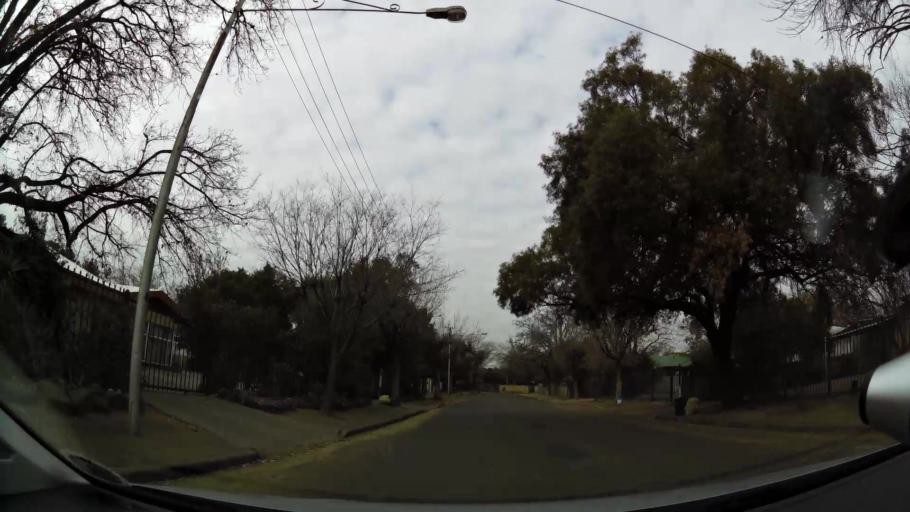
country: ZA
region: Orange Free State
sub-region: Mangaung Metropolitan Municipality
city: Bloemfontein
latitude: -29.1229
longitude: 26.1959
